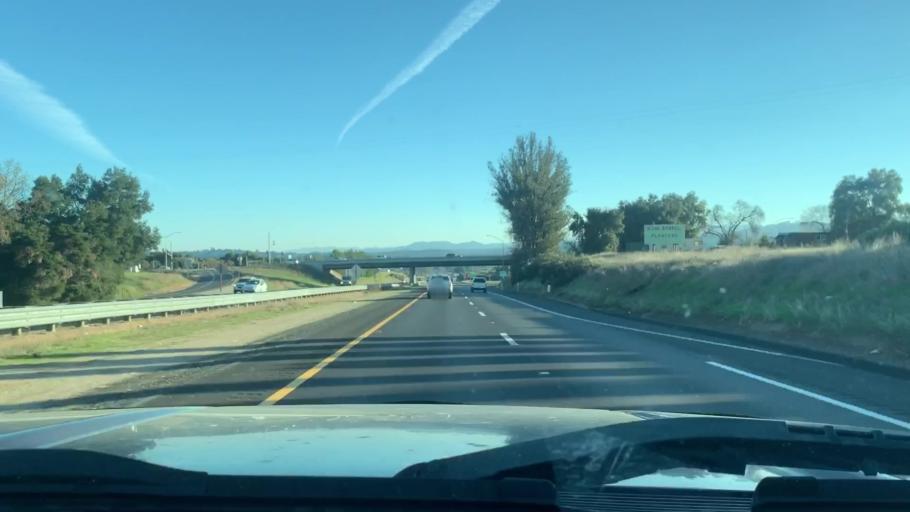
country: US
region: California
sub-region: San Luis Obispo County
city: Templeton
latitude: 35.5455
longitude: -120.7153
